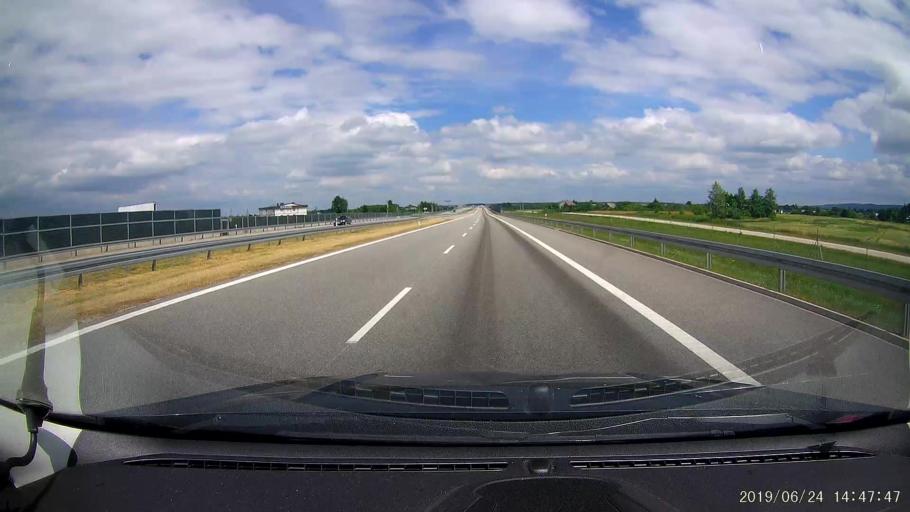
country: PL
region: Subcarpathian Voivodeship
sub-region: Powiat debicki
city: Zyrakow
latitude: 50.0815
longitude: 21.4089
